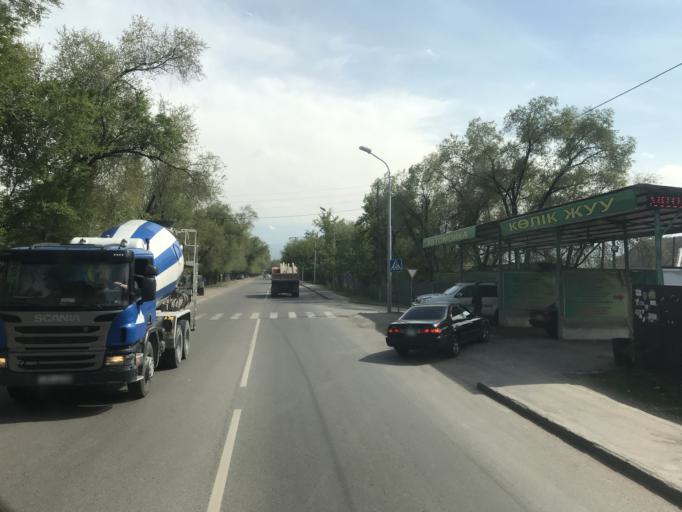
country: KZ
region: Almaty Qalasy
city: Almaty
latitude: 43.2444
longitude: 76.8046
